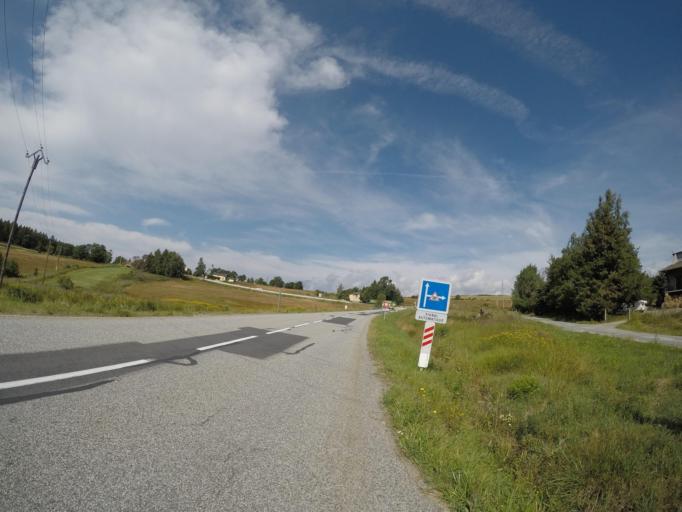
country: ES
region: Catalonia
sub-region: Provincia de Girona
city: Llivia
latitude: 42.4985
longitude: 2.0965
